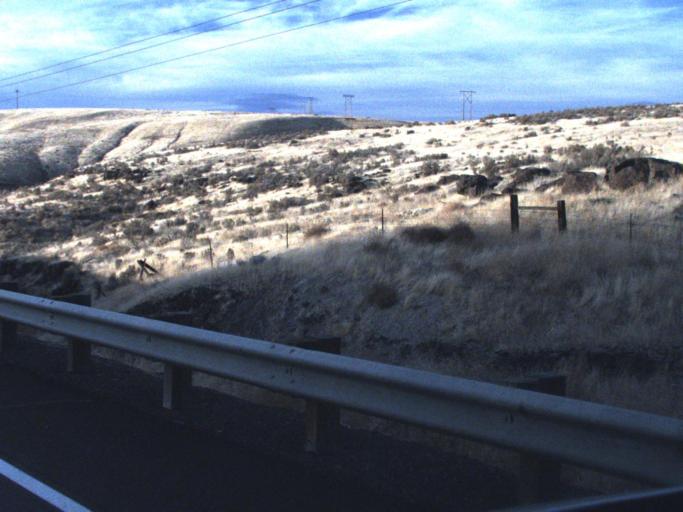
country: US
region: Washington
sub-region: Walla Walla County
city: Burbank
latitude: 46.0704
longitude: -118.7706
